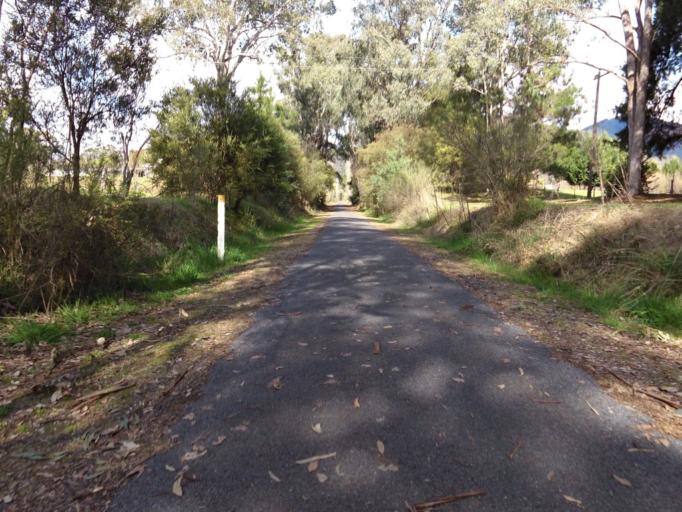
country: AU
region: Victoria
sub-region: Alpine
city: Mount Beauty
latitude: -36.7188
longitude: 146.9441
